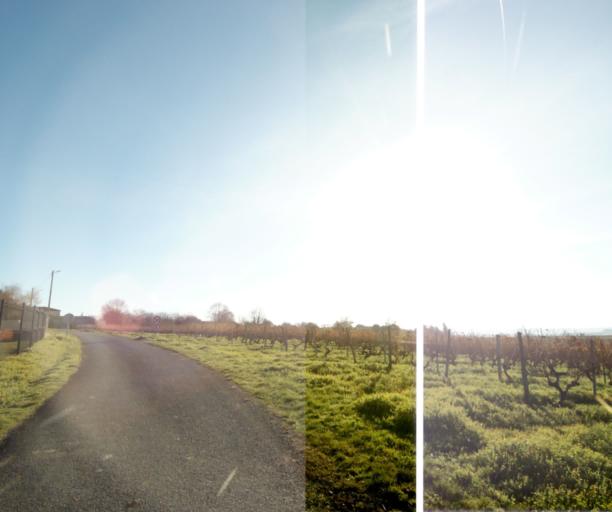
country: FR
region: Poitou-Charentes
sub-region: Departement de la Charente-Maritime
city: Cherac
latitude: 45.7056
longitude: -0.4531
